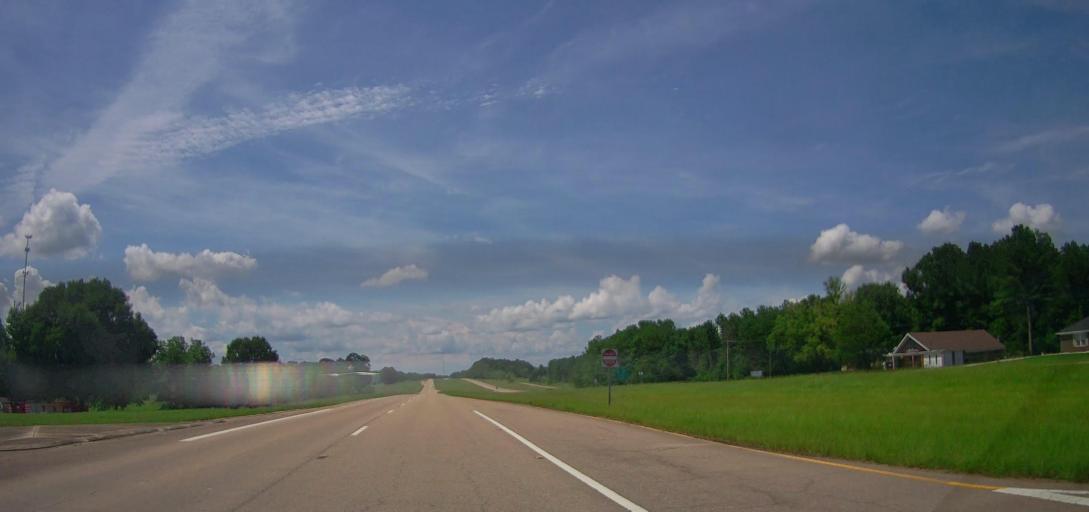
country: US
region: Mississippi
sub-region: Lee County
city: Nettleton
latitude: 33.9864
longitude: -88.6205
